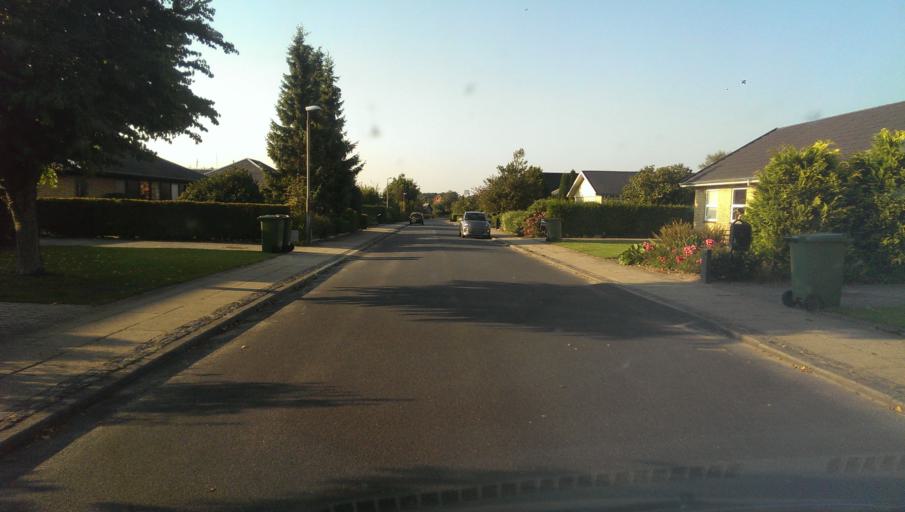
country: DK
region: South Denmark
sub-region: Esbjerg Kommune
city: Bramming
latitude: 55.4763
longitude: 8.7980
